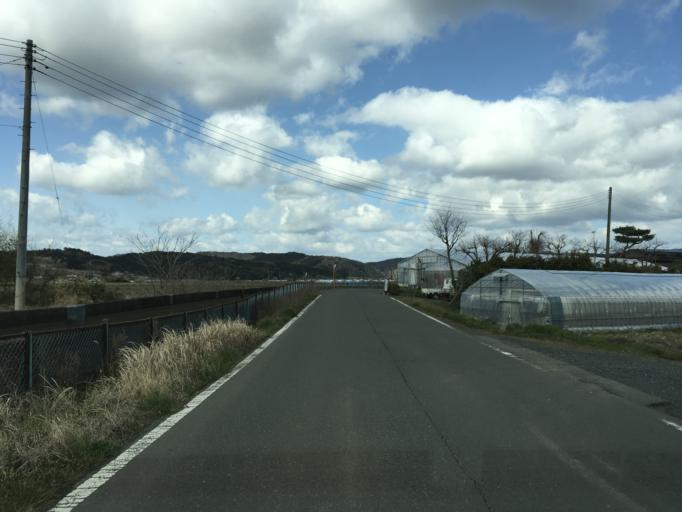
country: JP
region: Iwate
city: Ichinoseki
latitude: 38.7489
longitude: 141.2590
